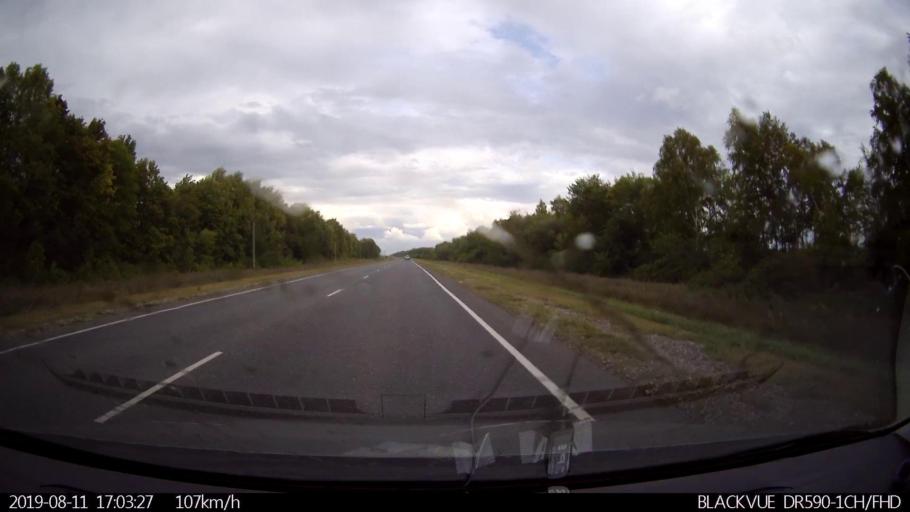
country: RU
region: Ulyanovsk
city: Mayna
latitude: 54.3029
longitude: 47.7405
